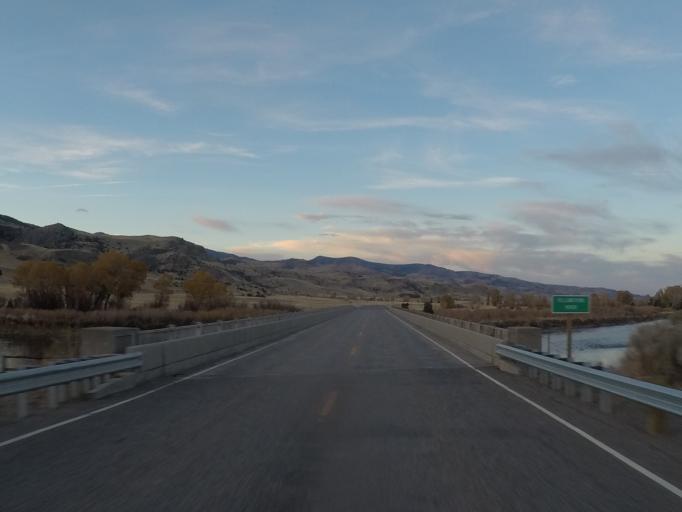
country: US
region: Montana
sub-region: Gallatin County
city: Bozeman
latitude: 45.2530
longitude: -110.8682
